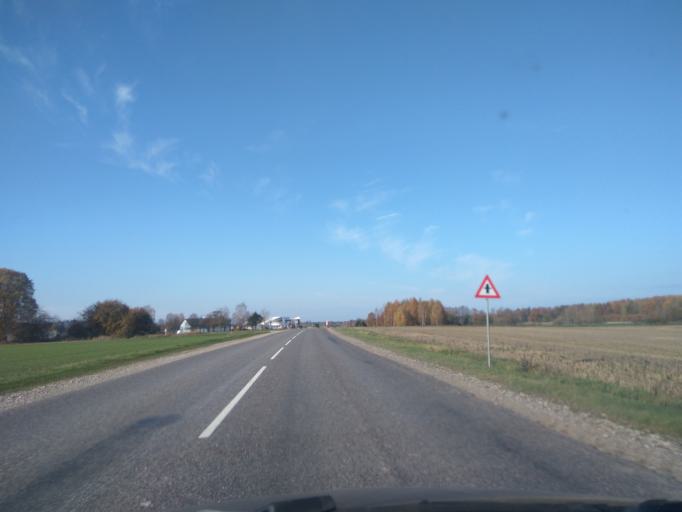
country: LV
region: Kuldigas Rajons
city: Kuldiga
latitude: 56.9954
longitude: 21.9050
